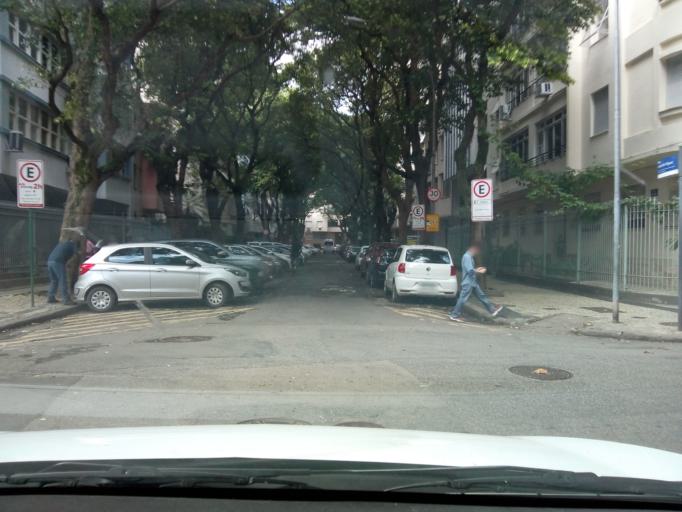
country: BR
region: Rio de Janeiro
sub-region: Rio De Janeiro
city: Rio de Janeiro
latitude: -22.9749
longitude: -43.1907
